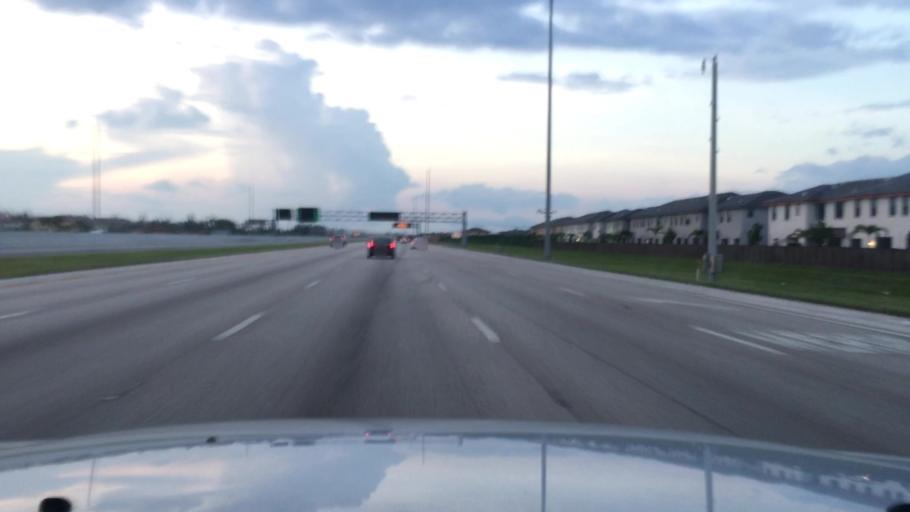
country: US
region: Florida
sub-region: Miami-Dade County
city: Palm Springs North
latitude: 25.9137
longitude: -80.3494
